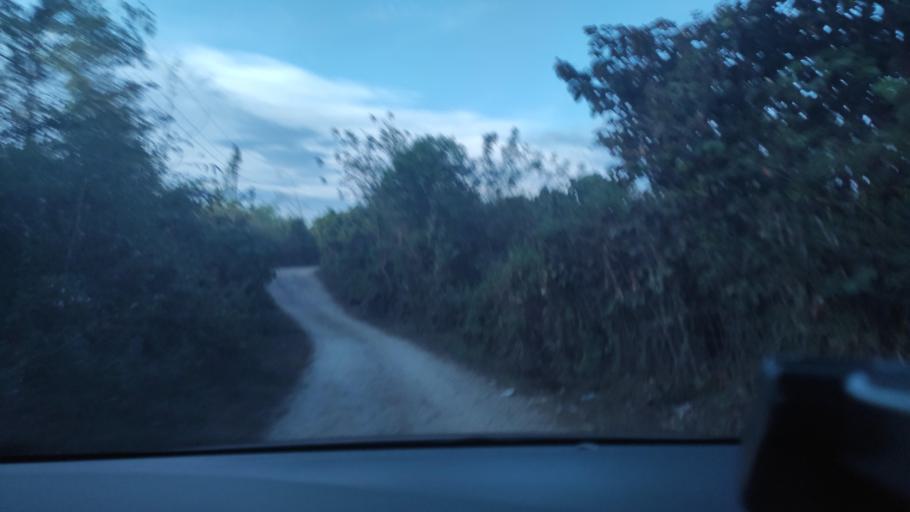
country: PH
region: Ilocos
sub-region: Province of Pangasinan
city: Balingasay
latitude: 16.3078
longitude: 119.8626
